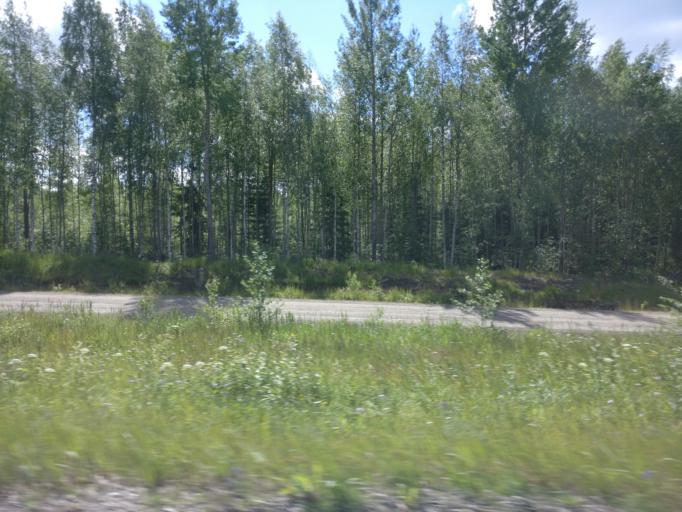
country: FI
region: Southern Savonia
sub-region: Savonlinna
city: Savonlinna
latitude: 61.8813
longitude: 29.0477
